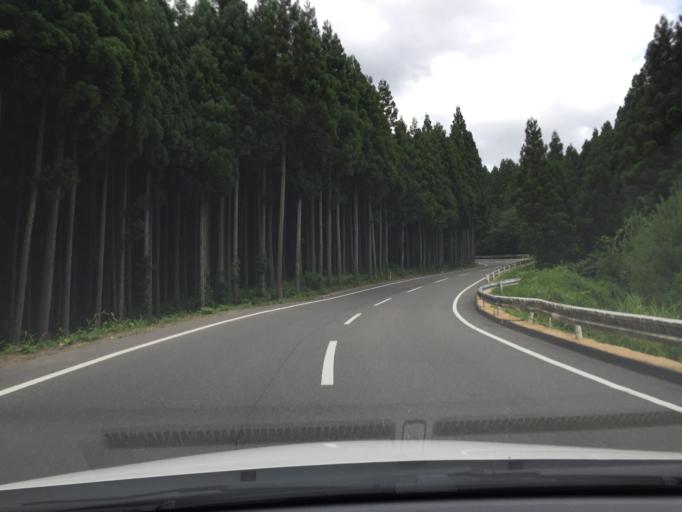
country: JP
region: Fukushima
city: Sukagawa
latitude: 37.1745
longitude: 140.1735
